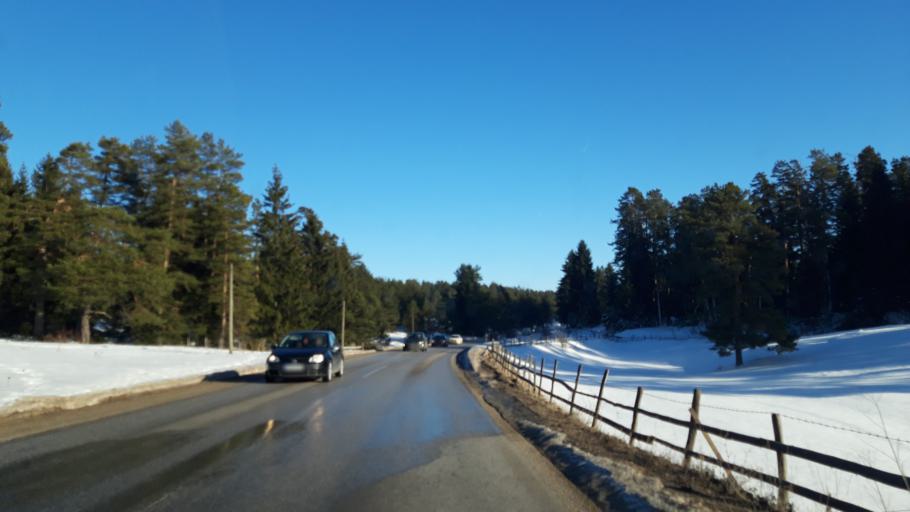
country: BA
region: Republika Srpska
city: Sokolac
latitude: 43.9192
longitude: 18.6918
